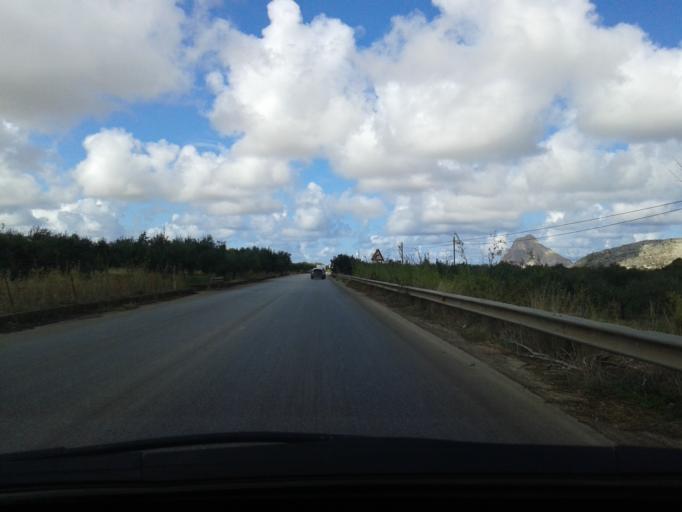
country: IT
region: Sicily
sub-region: Trapani
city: Castelluzzo
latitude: 38.0758
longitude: 12.7342
